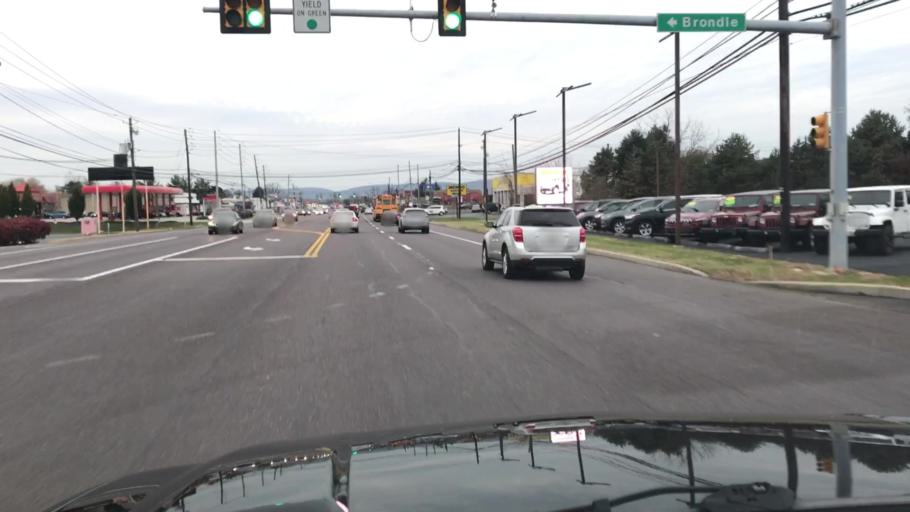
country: US
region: Pennsylvania
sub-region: Cumberland County
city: Mechanicsburg
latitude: 40.2426
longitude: -76.9904
